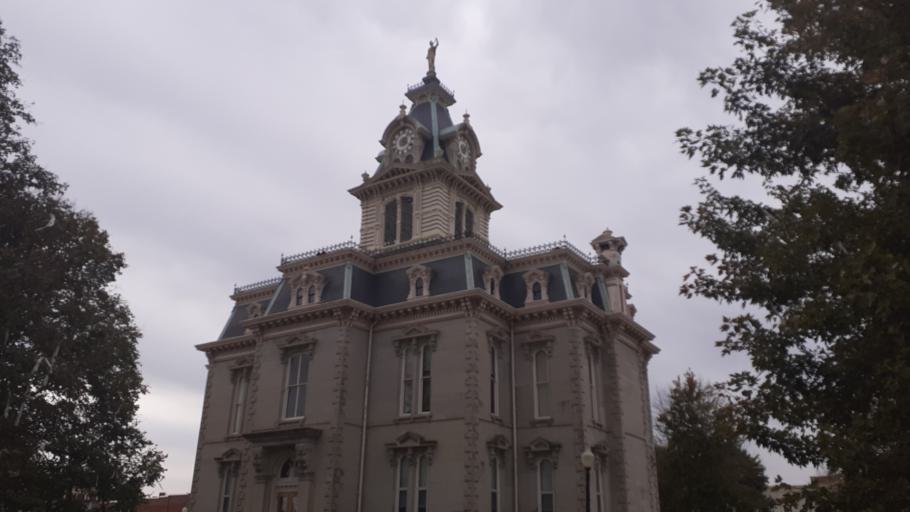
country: US
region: Iowa
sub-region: Davis County
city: Bloomfield
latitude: 40.7514
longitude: -92.4138
